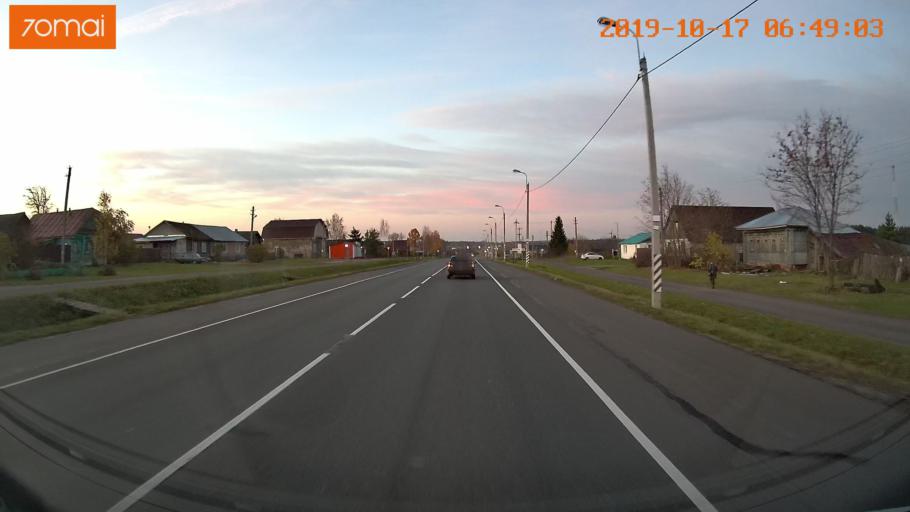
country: RU
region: Vladimir
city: Kideksha
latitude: 56.5165
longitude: 40.5526
